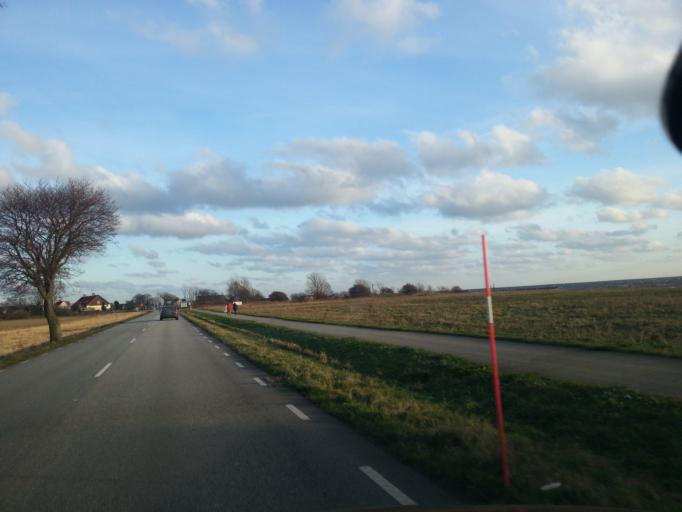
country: SE
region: Skane
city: Smygehamn
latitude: 55.3391
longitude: 13.3533
